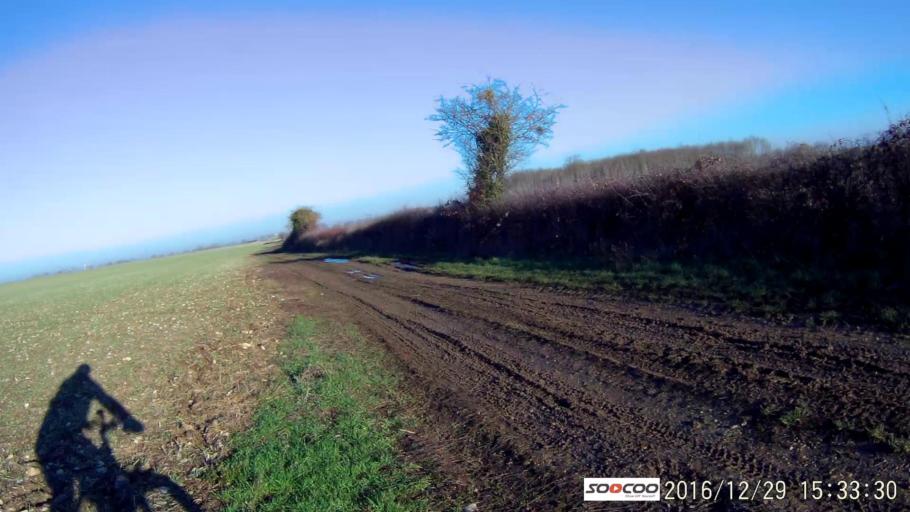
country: FR
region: Centre
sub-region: Departement de l'Indre
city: Neuvy-Pailloux
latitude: 46.9387
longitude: 1.8322
